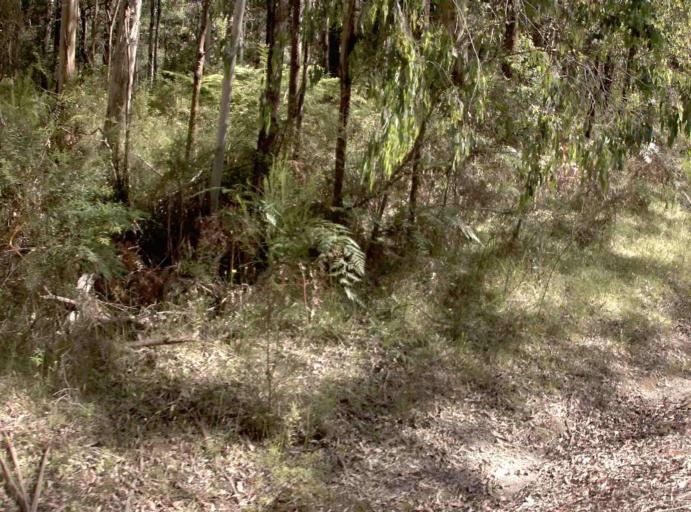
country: AU
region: New South Wales
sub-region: Bombala
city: Bombala
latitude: -37.3040
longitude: 148.7042
